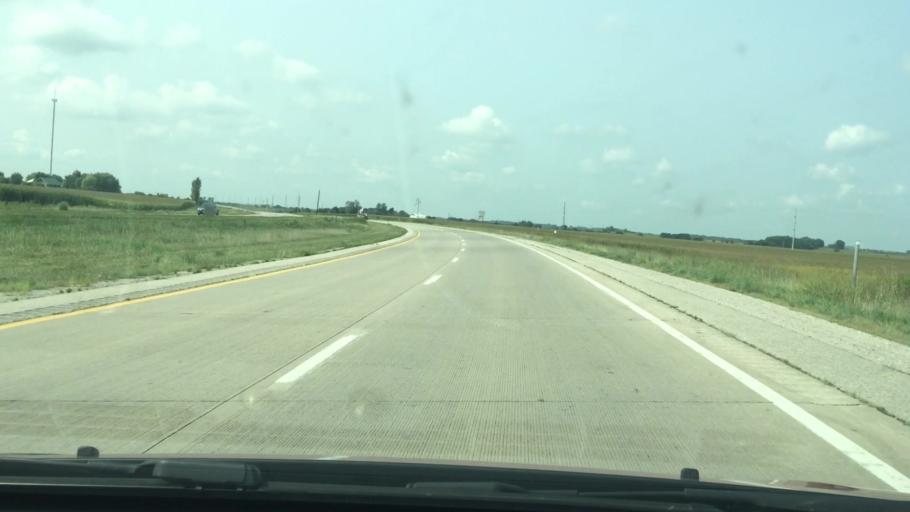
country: US
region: Iowa
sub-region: Muscatine County
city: Wilton
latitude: 41.4982
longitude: -90.9698
